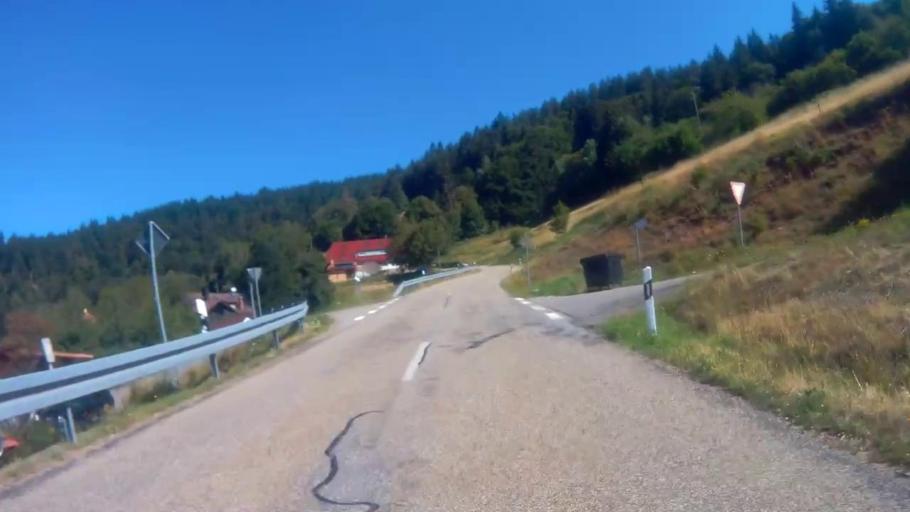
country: DE
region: Baden-Wuerttemberg
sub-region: Freiburg Region
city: Sulzburg
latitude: 47.7655
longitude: 7.7530
